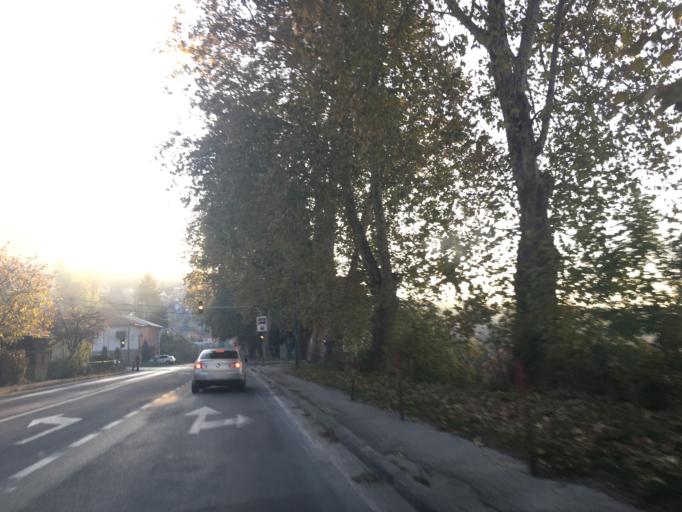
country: BA
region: Federation of Bosnia and Herzegovina
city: Kobilja Glava
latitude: 43.8531
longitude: 18.4341
